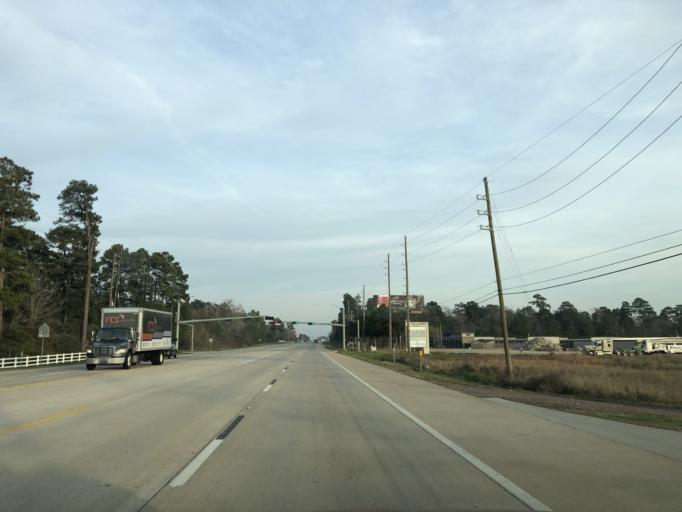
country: US
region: Texas
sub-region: Montgomery County
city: Pinehurst
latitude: 30.2211
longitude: -95.5938
